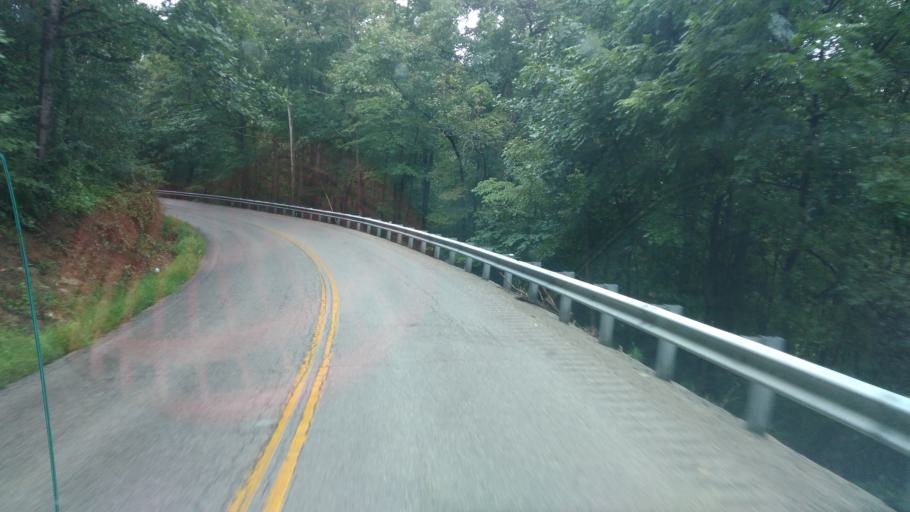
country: US
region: Kentucky
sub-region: Fleming County
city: Flemingsburg
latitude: 38.4528
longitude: -83.5216
